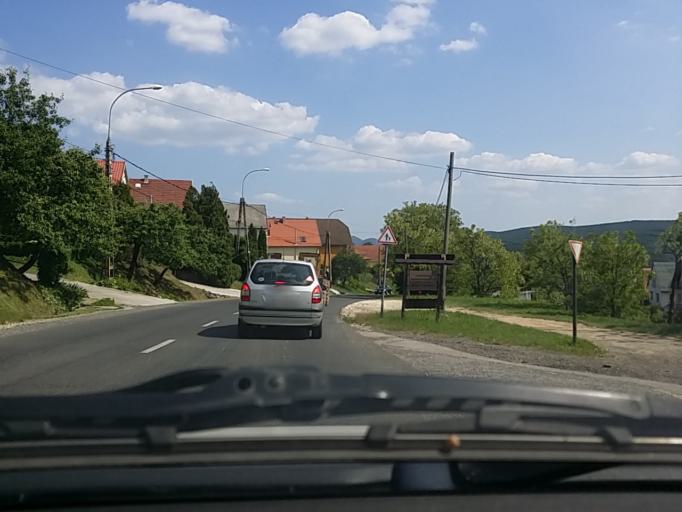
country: HU
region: Pest
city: Pilisszentkereszt
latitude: 47.6980
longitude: 18.8995
